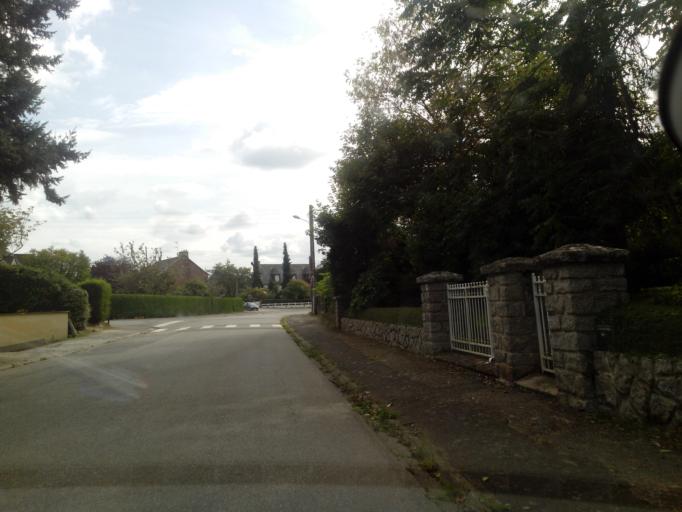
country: FR
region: Brittany
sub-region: Departement du Morbihan
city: Mauron
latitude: 48.0791
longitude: -2.2881
